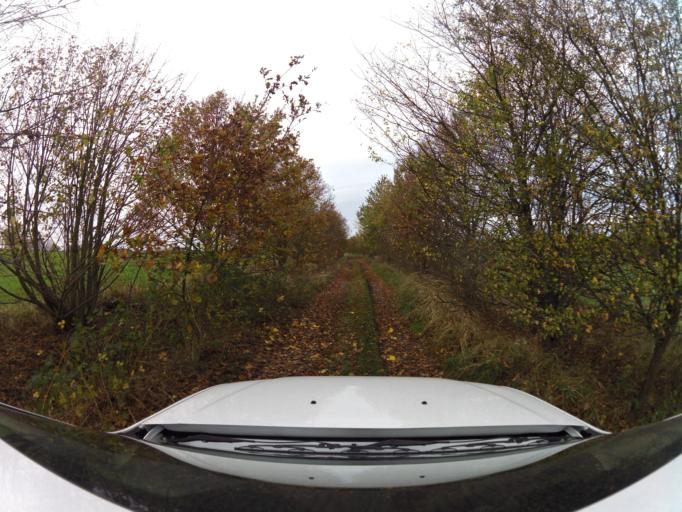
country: PL
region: West Pomeranian Voivodeship
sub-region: Powiat gryficki
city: Cerkwica
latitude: 54.0500
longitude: 15.0998
